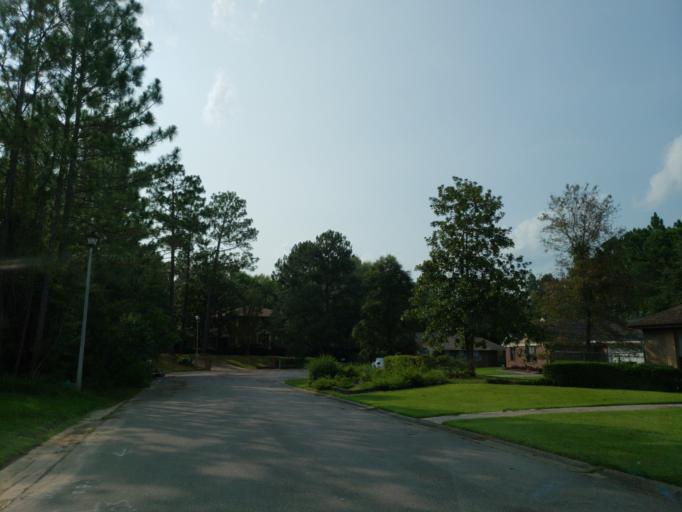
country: US
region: Mississippi
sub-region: Lamar County
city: West Hattiesburg
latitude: 31.3181
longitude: -89.3499
